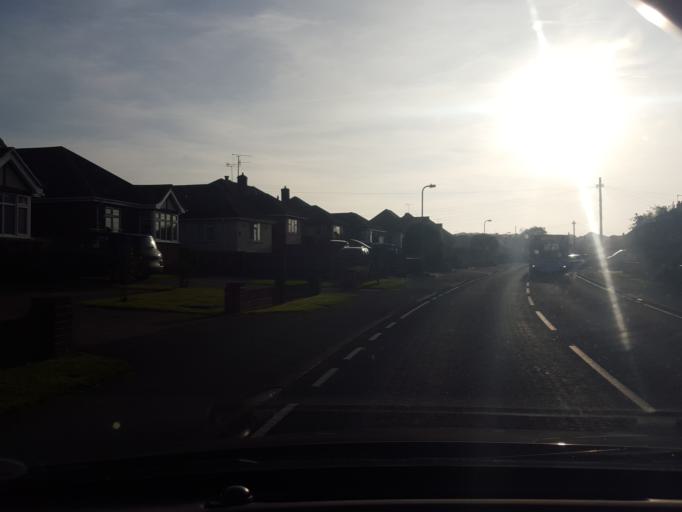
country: GB
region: England
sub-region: Essex
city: Walton-on-the-Naze
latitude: 51.8459
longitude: 1.2633
